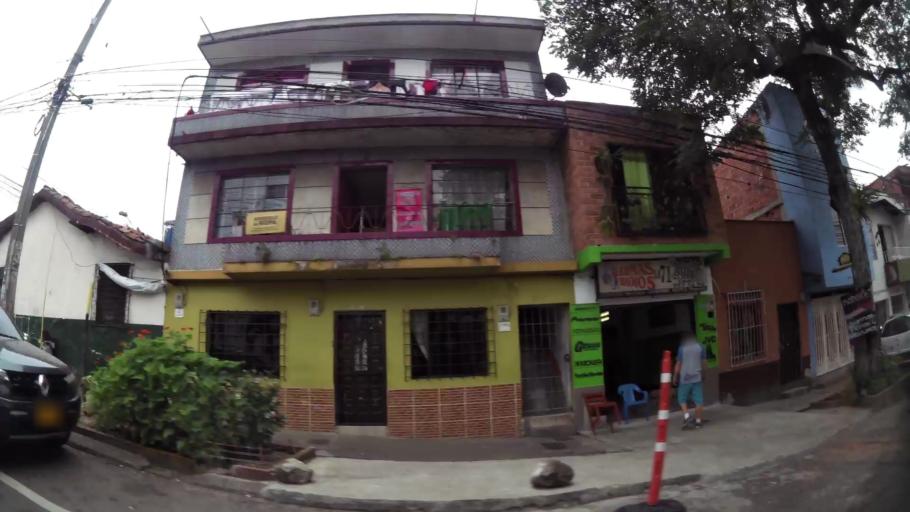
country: CO
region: Antioquia
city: Medellin
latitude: 6.2675
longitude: -75.5620
